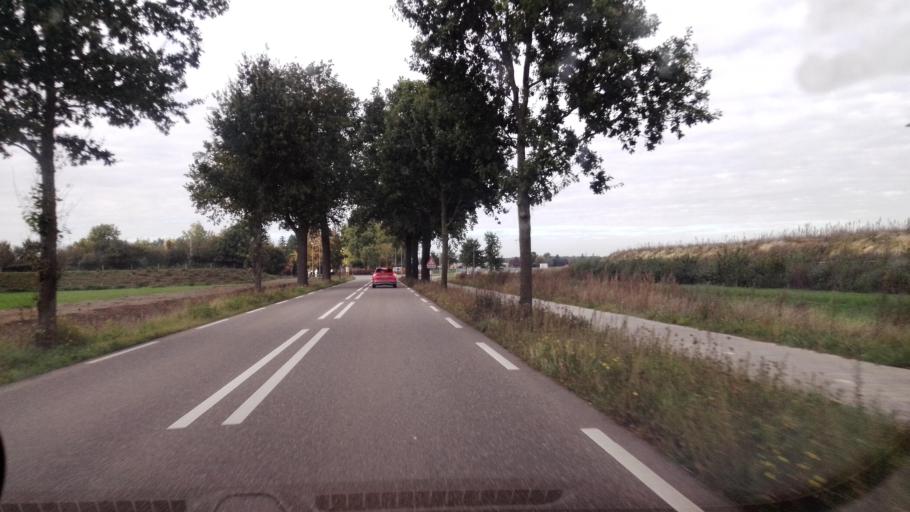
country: NL
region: Limburg
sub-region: Gemeente Peel en Maas
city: Maasbree
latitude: 51.4318
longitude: 6.0927
